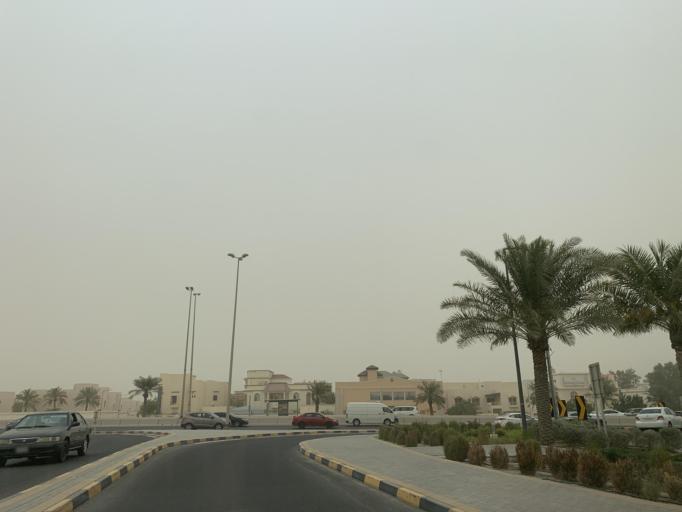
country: BH
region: Central Governorate
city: Madinat Hamad
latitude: 26.1377
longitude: 50.5188
